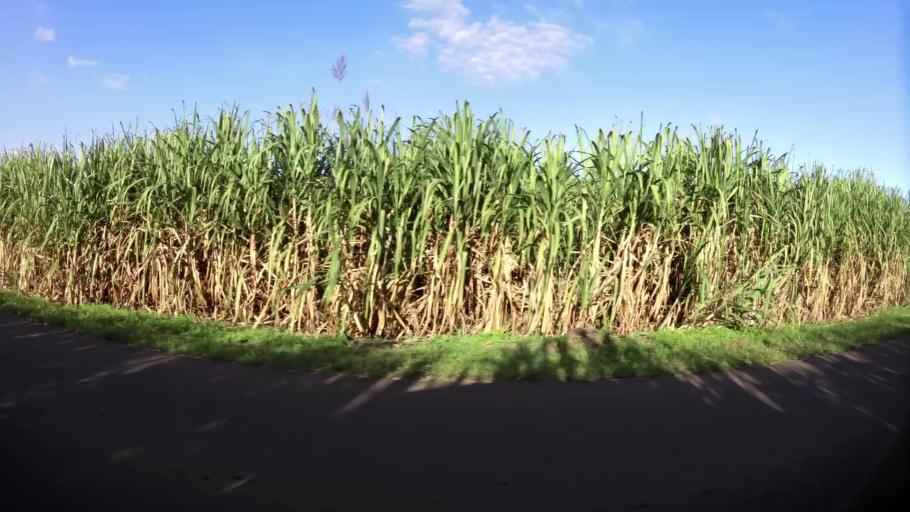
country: RE
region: Reunion
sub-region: Reunion
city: Saint-Louis
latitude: -21.2668
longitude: 55.3794
